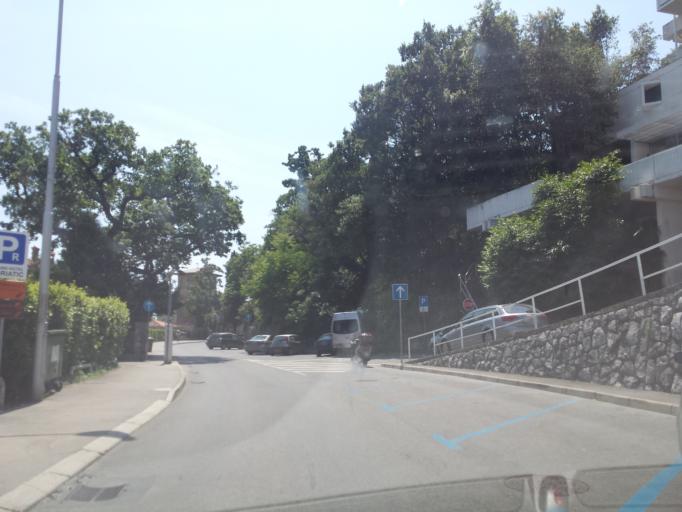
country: HR
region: Primorsko-Goranska
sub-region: Grad Opatija
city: Opatija
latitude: 45.3258
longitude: 14.2990
